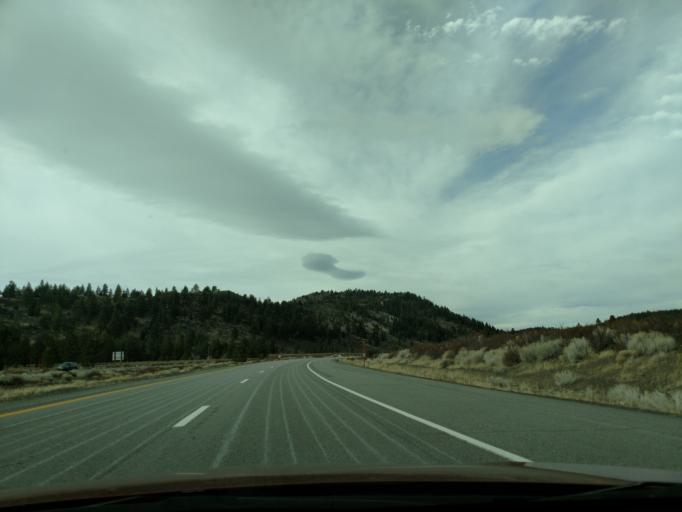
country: US
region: California
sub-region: Mono County
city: Mammoth Lakes
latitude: 37.6440
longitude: -118.9208
